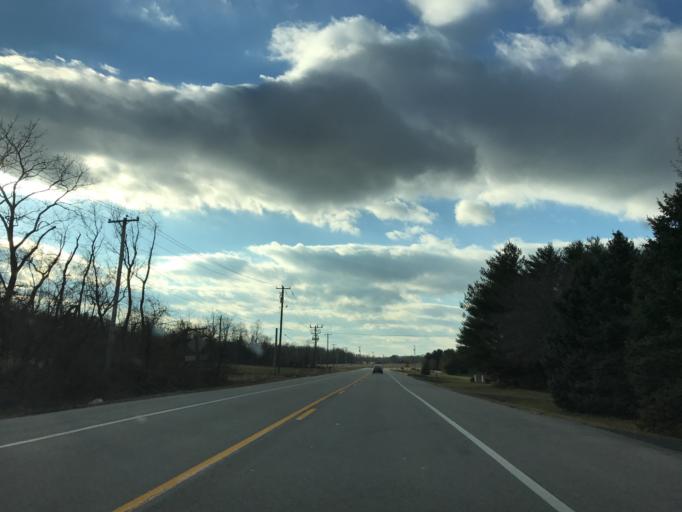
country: US
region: Maryland
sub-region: Cecil County
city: North East
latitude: 39.6558
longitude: -75.9827
